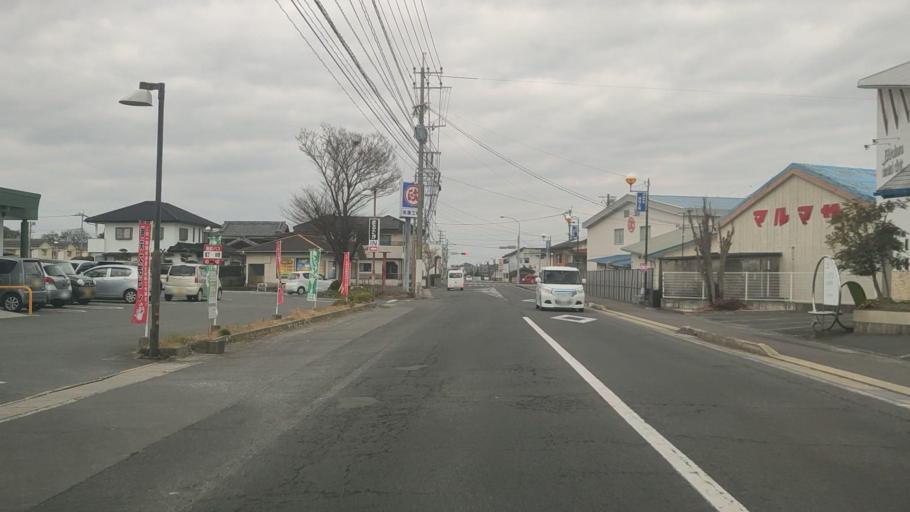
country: JP
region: Nagasaki
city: Shimabara
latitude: 32.8614
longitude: 130.3256
